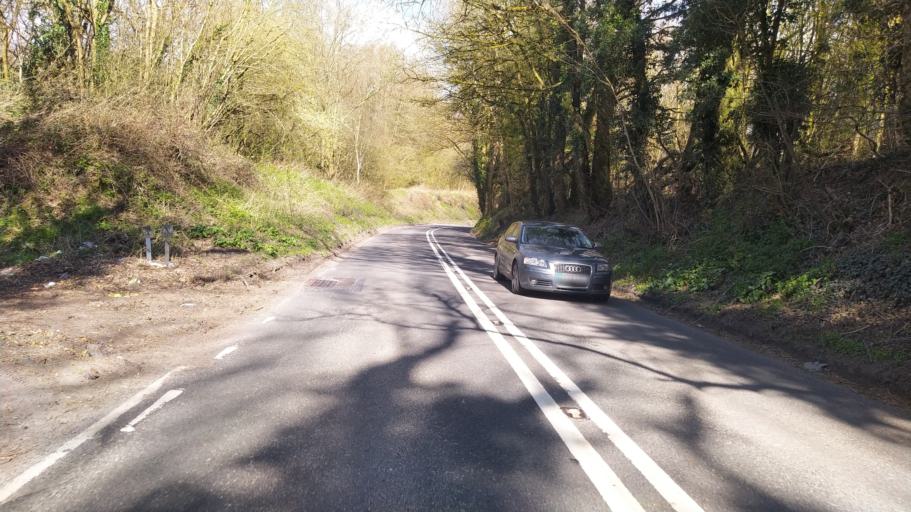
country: GB
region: England
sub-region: Dorset
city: Shaftesbury
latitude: 51.0264
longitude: -2.1898
